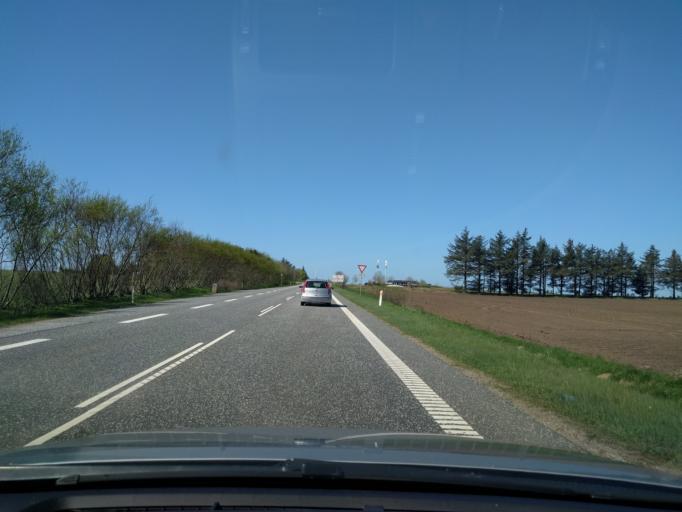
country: DK
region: Central Jutland
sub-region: Ringkobing-Skjern Kommune
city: Videbaek
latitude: 56.0862
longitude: 8.5122
